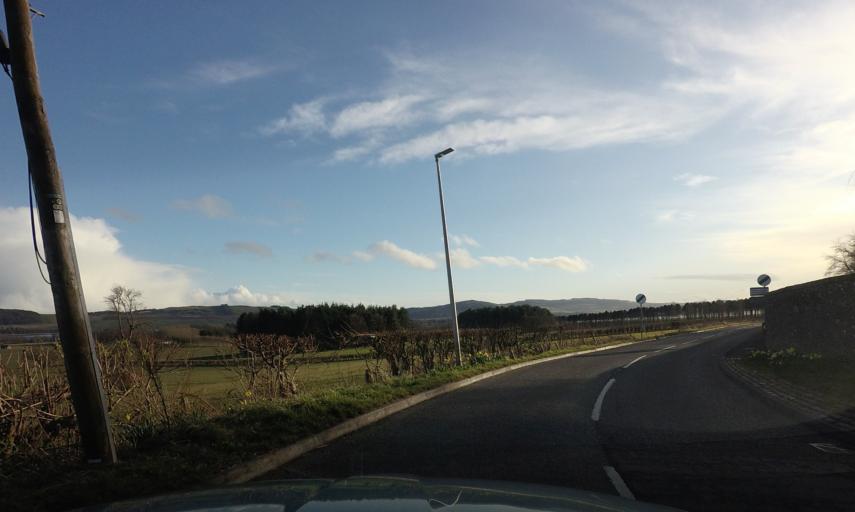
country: GB
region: Scotland
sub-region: Perth and Kinross
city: Errol
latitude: 56.3901
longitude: -3.2152
